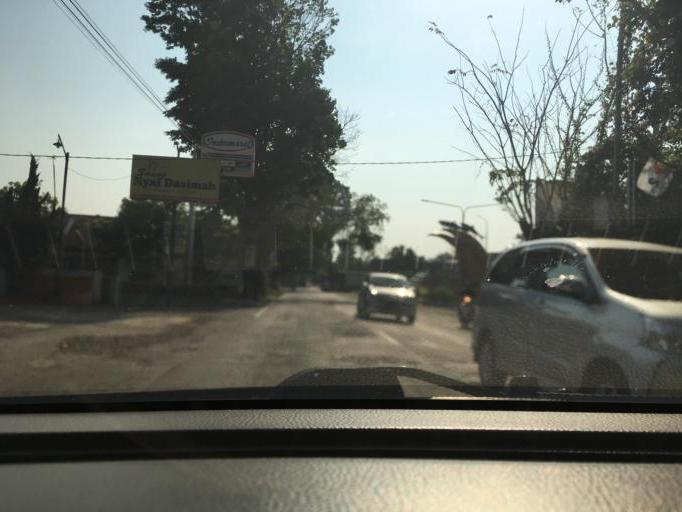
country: ID
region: West Java
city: Sumber
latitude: -6.8498
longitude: 108.5074
